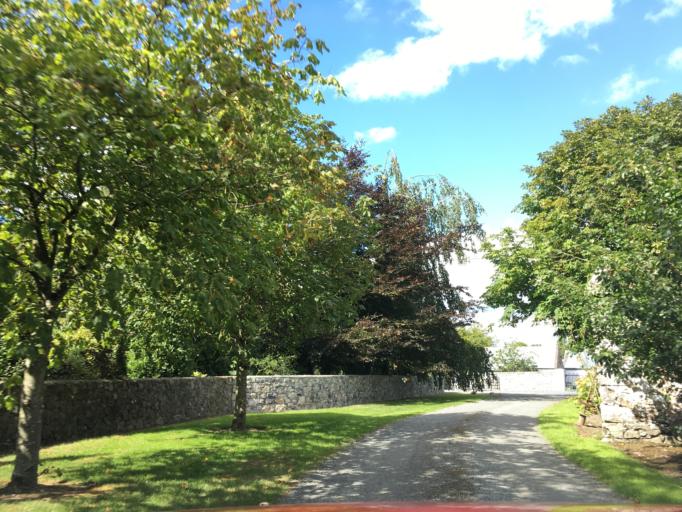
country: IE
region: Munster
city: Cashel
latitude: 52.4619
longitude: -7.9418
